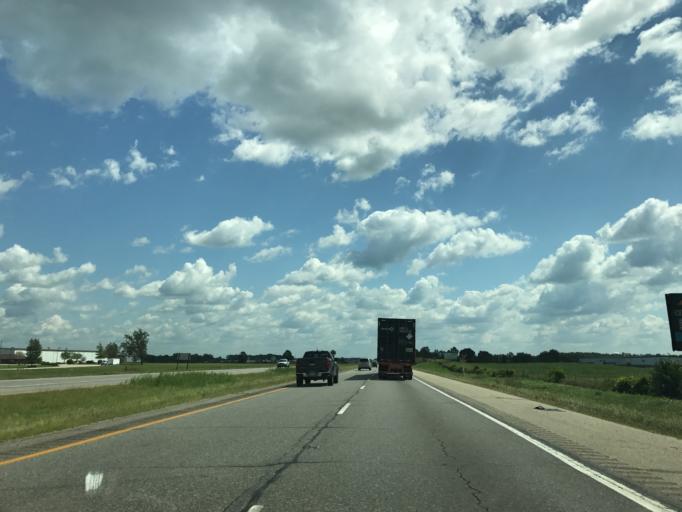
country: US
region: Indiana
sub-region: Marshall County
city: Plymouth
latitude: 41.3613
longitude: -86.3470
